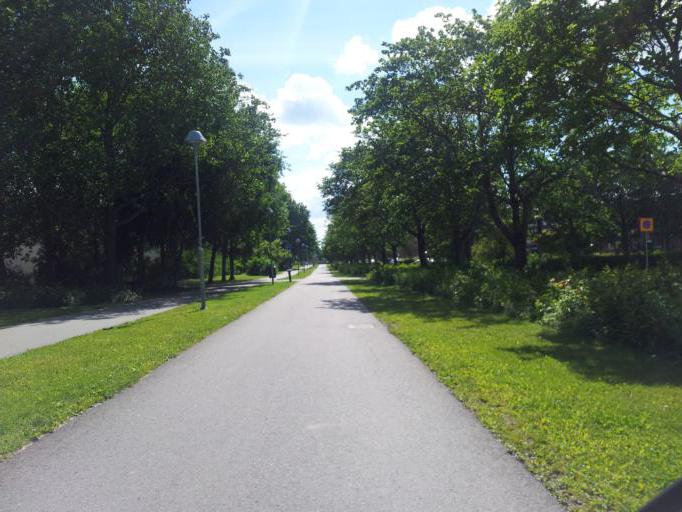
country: SE
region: Uppsala
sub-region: Uppsala Kommun
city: Uppsala
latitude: 59.8726
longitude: 17.6611
